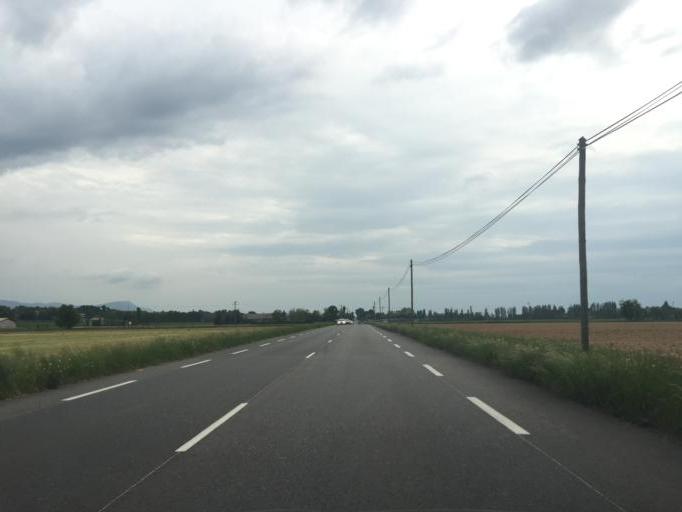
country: FR
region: Rhone-Alpes
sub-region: Departement de la Drome
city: Alixan
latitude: 44.9903
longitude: 5.0321
